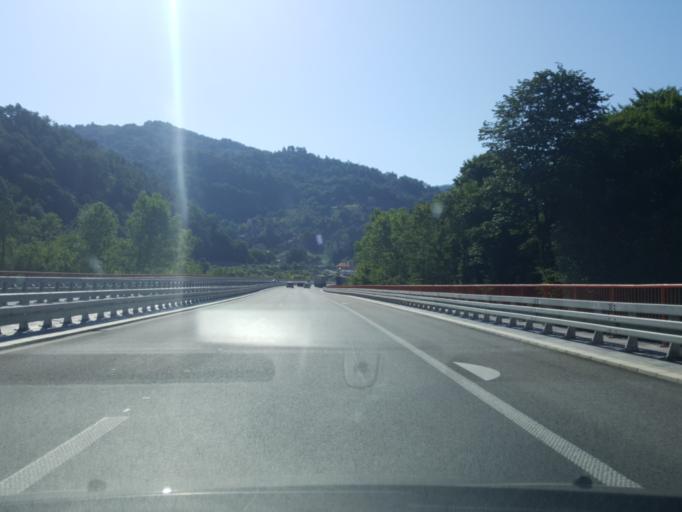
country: RS
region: Central Serbia
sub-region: Jablanicki Okrug
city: Vlasotince
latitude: 42.8645
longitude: 22.1123
